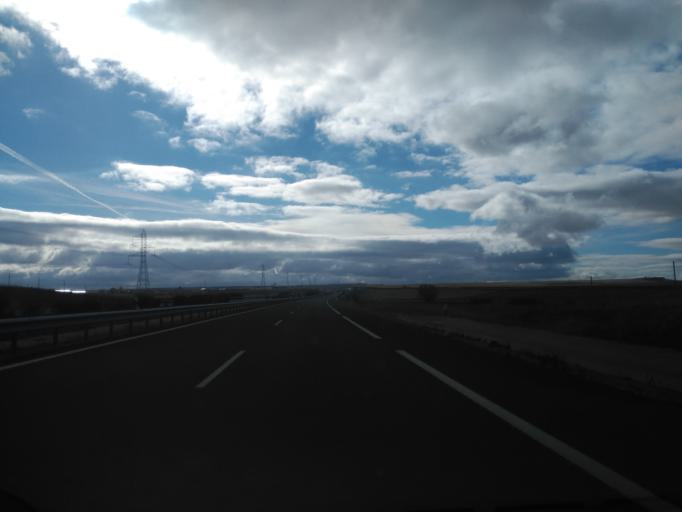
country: ES
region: Castille and Leon
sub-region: Provincia de Palencia
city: Abia de las Torres
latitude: 42.3828
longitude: -4.3861
